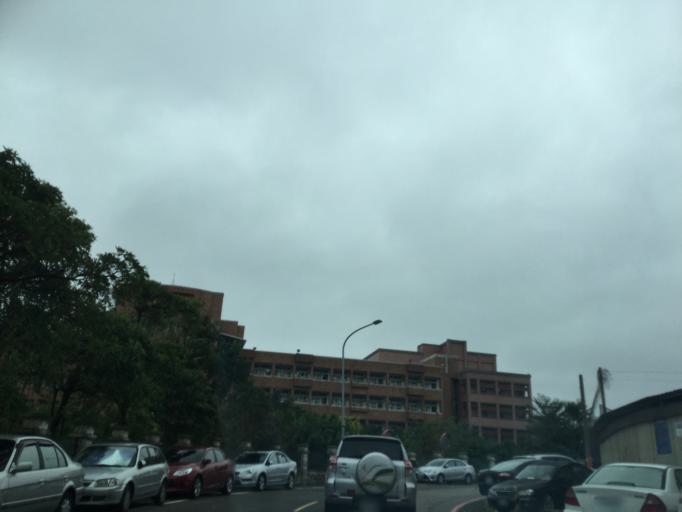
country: TW
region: Taiwan
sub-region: Hsinchu
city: Hsinchu
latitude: 24.7988
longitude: 121.0007
